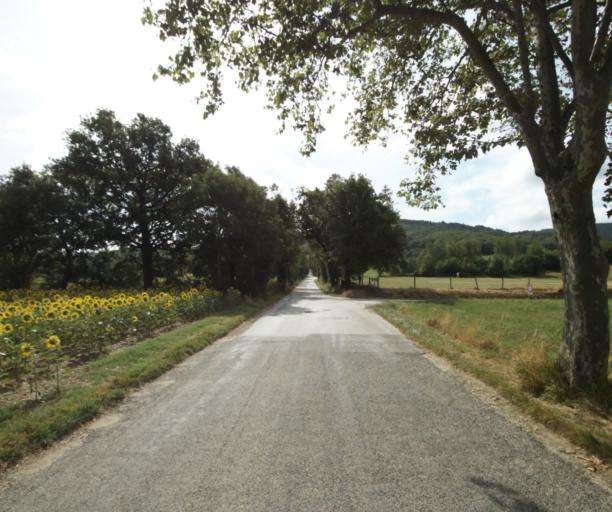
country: FR
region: Midi-Pyrenees
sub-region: Departement du Tarn
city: Dourgne
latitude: 43.4692
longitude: 2.1037
